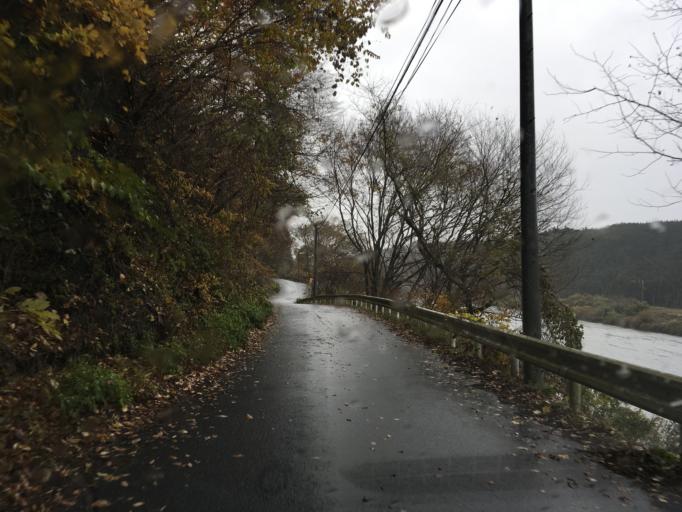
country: JP
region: Iwate
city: Ichinoseki
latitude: 38.8101
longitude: 141.2513
